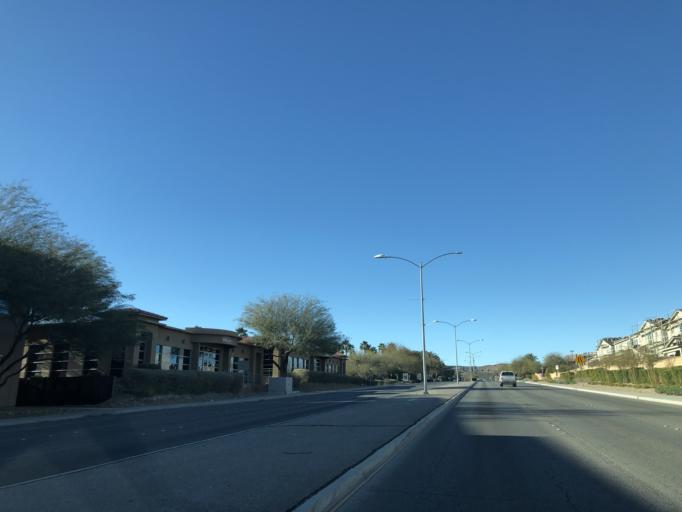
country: US
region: Nevada
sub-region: Clark County
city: Whitney
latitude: 36.0137
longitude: -115.0595
